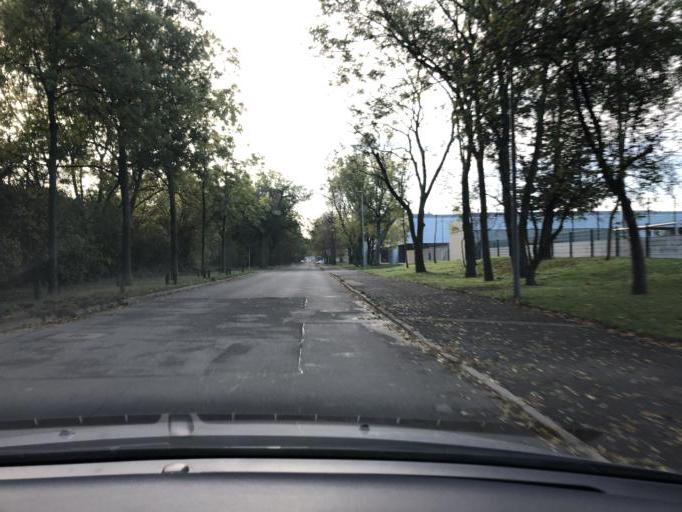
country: DE
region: Saxony
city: Leipzig
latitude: 51.3449
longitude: 12.3417
